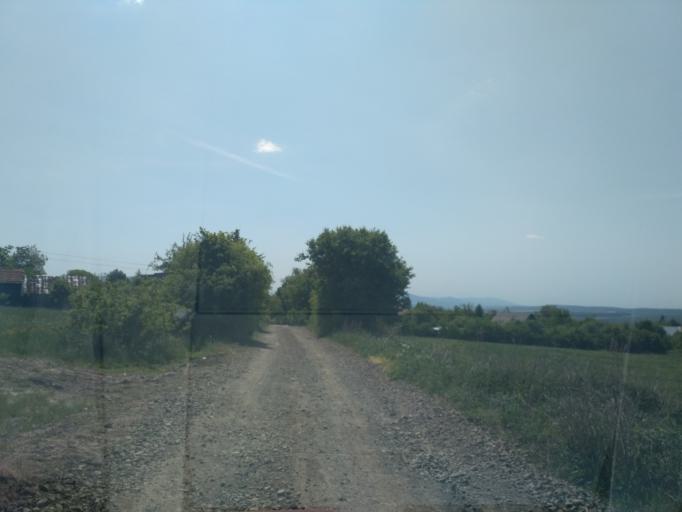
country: SK
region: Kosicky
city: Kosice
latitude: 48.8305
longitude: 21.4505
